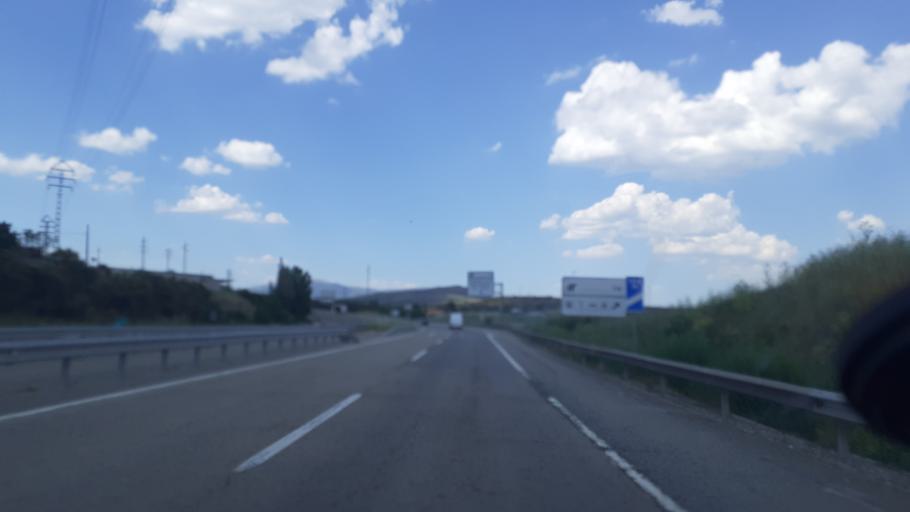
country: ES
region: Madrid
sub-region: Provincia de Madrid
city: Buitrago del Lozoya
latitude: 40.9995
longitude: -3.6395
